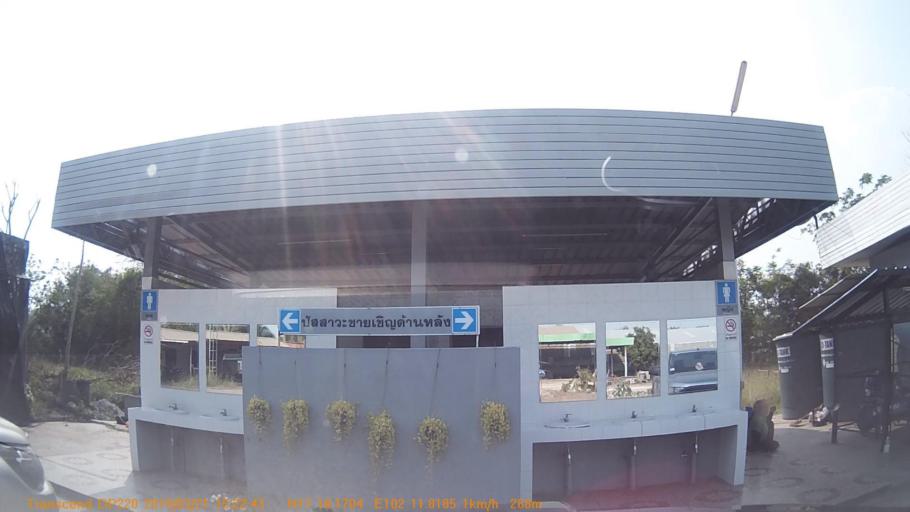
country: TH
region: Changwat Nong Bua Lamphu
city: Na Klang
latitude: 17.3028
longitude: 102.1968
